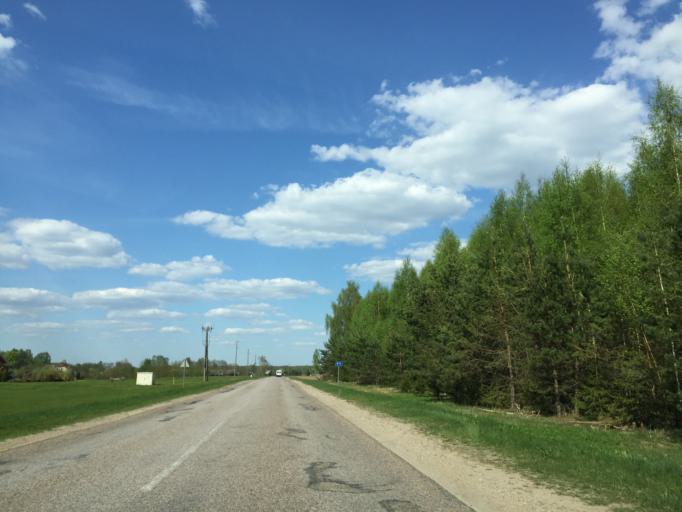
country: LV
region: Limbazu Rajons
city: Limbazi
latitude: 57.4236
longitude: 24.7065
